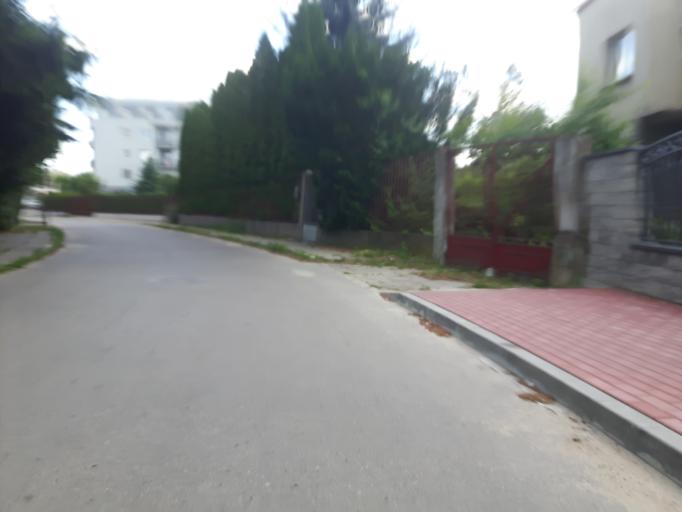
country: PL
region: Masovian Voivodeship
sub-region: Powiat wolominski
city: Zabki
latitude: 52.2933
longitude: 21.1184
